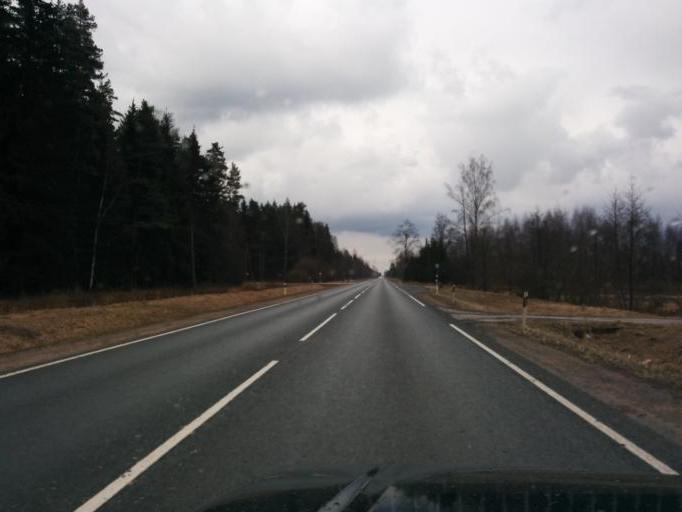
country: LV
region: Ozolnieku
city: Ozolnieki
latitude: 56.7145
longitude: 23.8341
